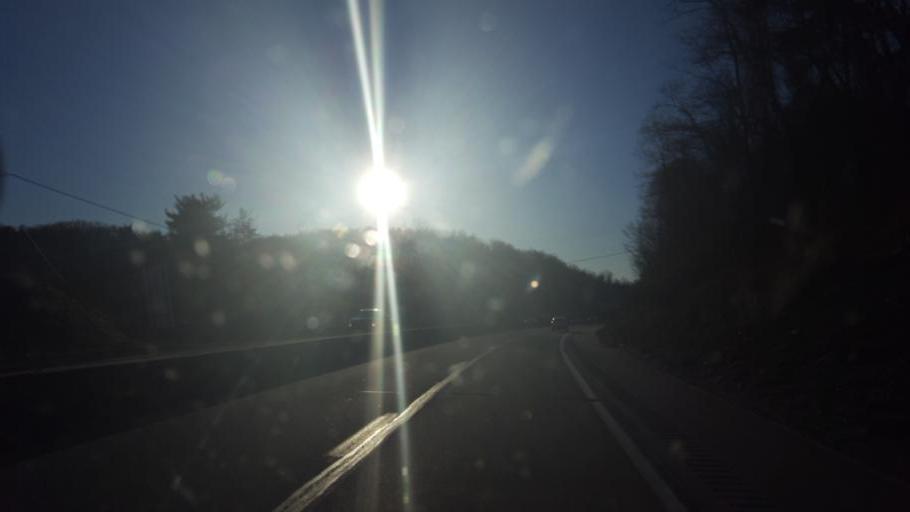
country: US
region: Pennsylvania
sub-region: Washington County
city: Speers
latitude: 40.1073
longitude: -79.9011
